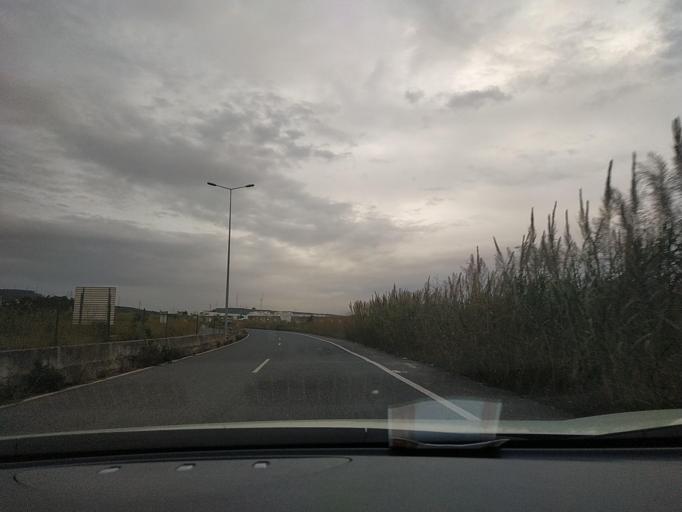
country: PT
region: Lisbon
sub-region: Loures
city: Santo Antao do Tojal
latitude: 38.8546
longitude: -9.1452
